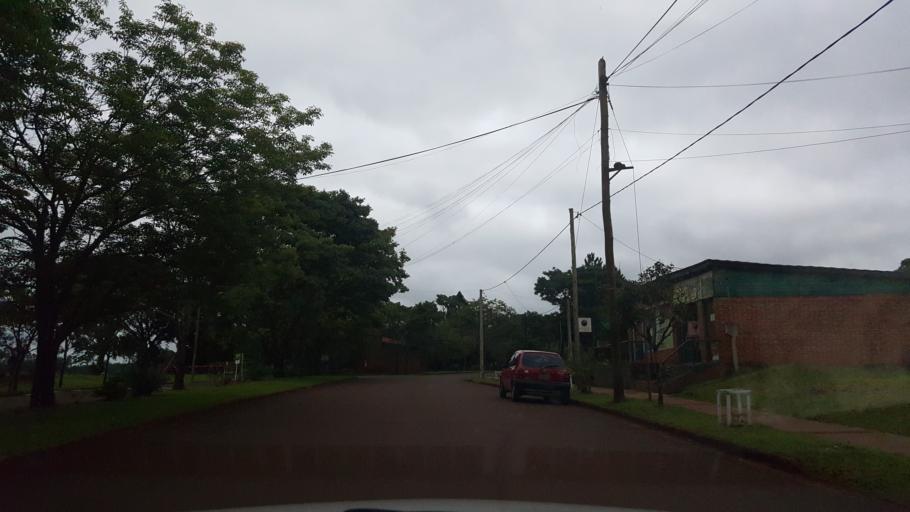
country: AR
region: Misiones
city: Ruiz de Montoya
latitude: -26.9768
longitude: -55.0512
